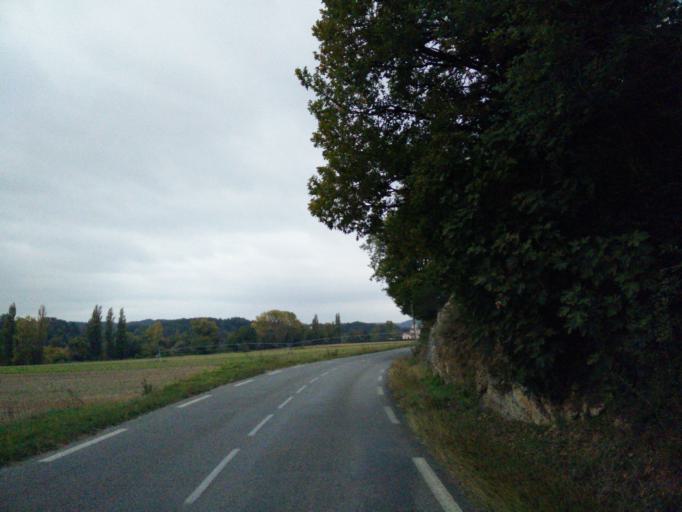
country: FR
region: Midi-Pyrenees
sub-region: Departement du Lot
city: Cahors
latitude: 44.4605
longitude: 1.4938
